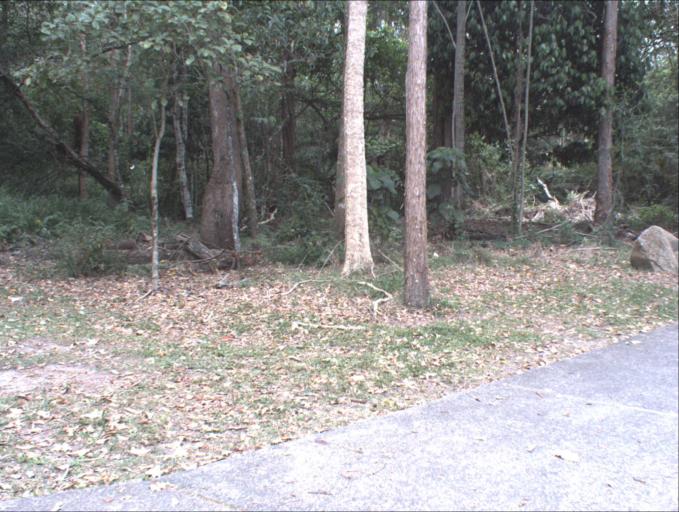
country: AU
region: Queensland
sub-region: Logan
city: Beenleigh
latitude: -27.6569
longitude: 153.2061
